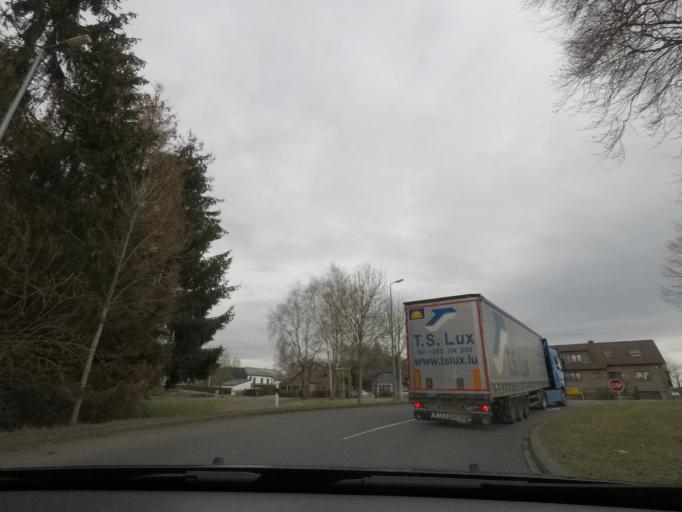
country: LU
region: Diekirch
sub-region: Canton de Wiltz
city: Winseler
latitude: 50.0141
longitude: 5.8827
